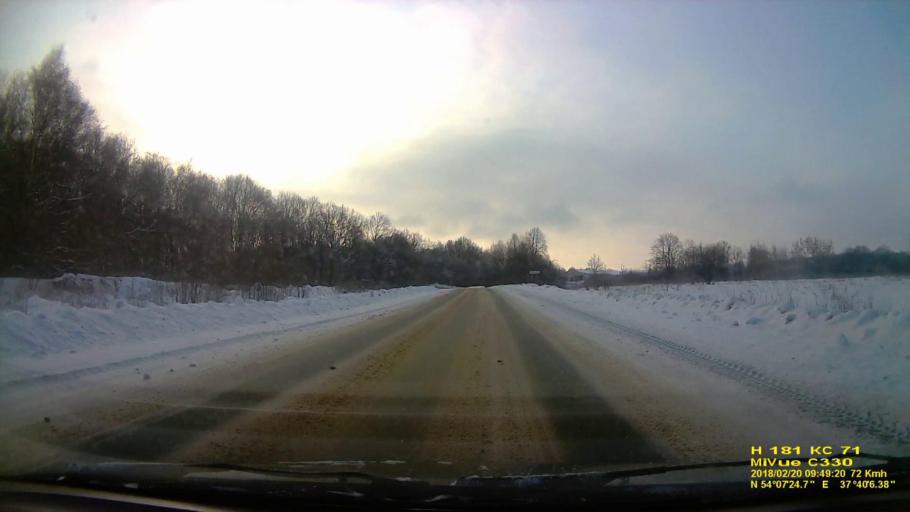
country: RU
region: Tula
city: Skuratovskiy
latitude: 54.1233
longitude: 37.6686
